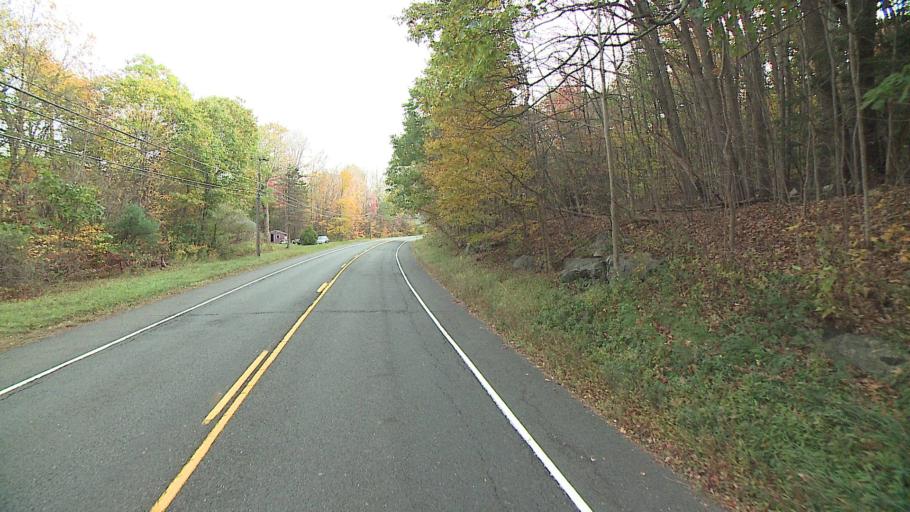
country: US
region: Connecticut
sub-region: Litchfield County
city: Winchester Center
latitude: 41.9526
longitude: -73.1153
